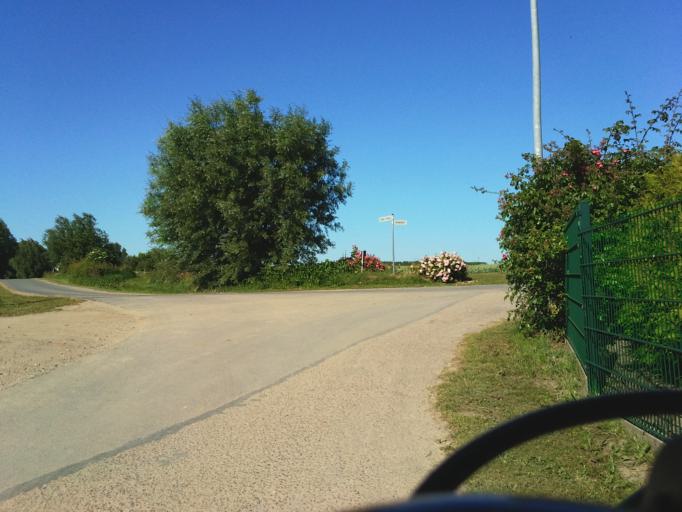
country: DE
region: Mecklenburg-Vorpommern
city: Monchhagen
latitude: 54.1586
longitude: 12.1953
